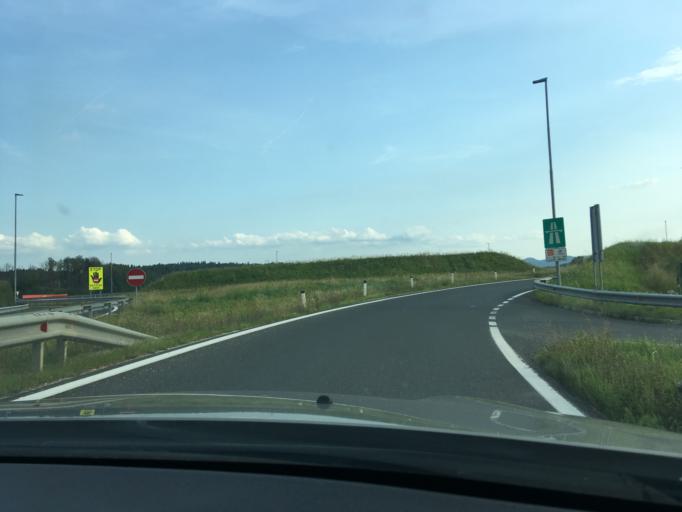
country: SI
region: Ivancna Gorica
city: Ivancna Gorica
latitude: 45.9355
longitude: 14.8057
